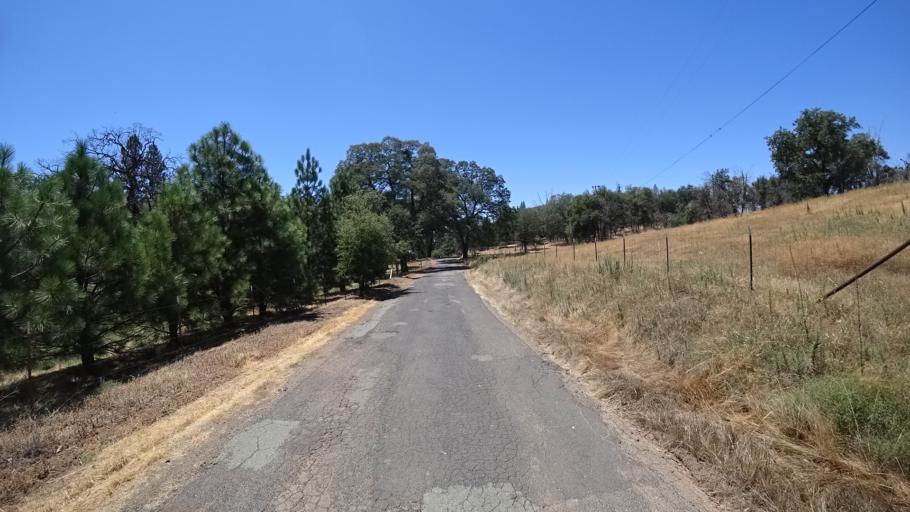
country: US
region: California
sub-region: Calaveras County
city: Mountain Ranch
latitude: 38.2904
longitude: -120.6010
